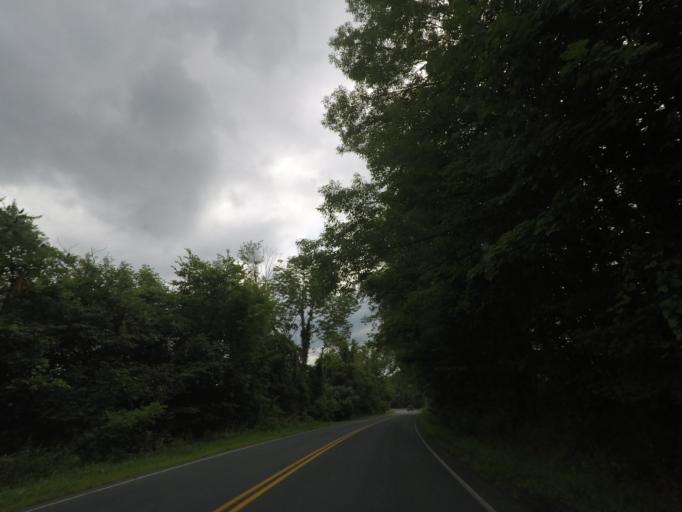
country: US
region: New York
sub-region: Saratoga County
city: Stillwater
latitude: 42.8739
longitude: -73.5588
